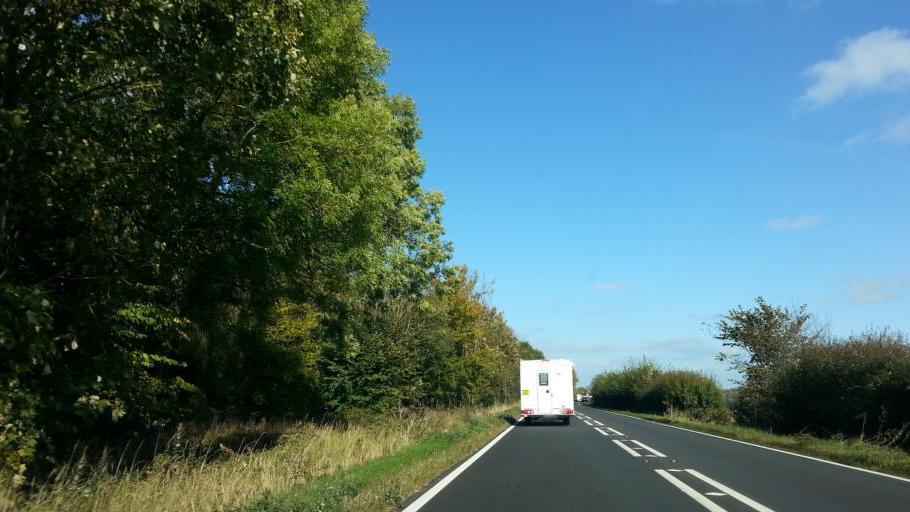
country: GB
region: England
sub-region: Northamptonshire
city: Oundle
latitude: 52.4418
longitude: -0.4712
